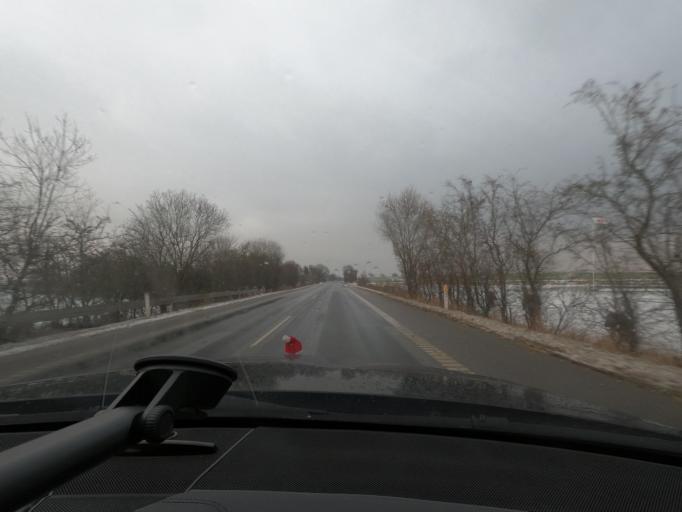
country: DK
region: South Denmark
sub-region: Sonderborg Kommune
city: Horuphav
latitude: 54.8924
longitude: 9.9706
